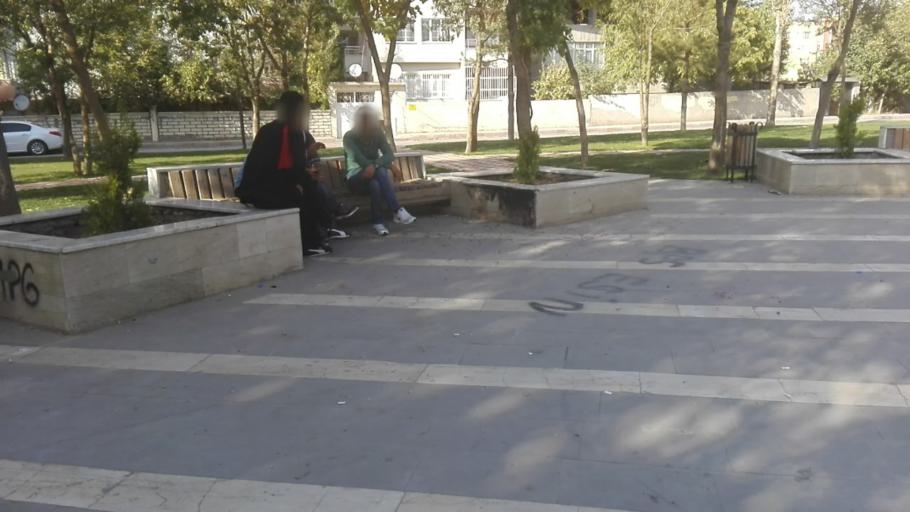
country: TR
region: Batman
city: Batman
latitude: 37.8949
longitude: 41.1253
